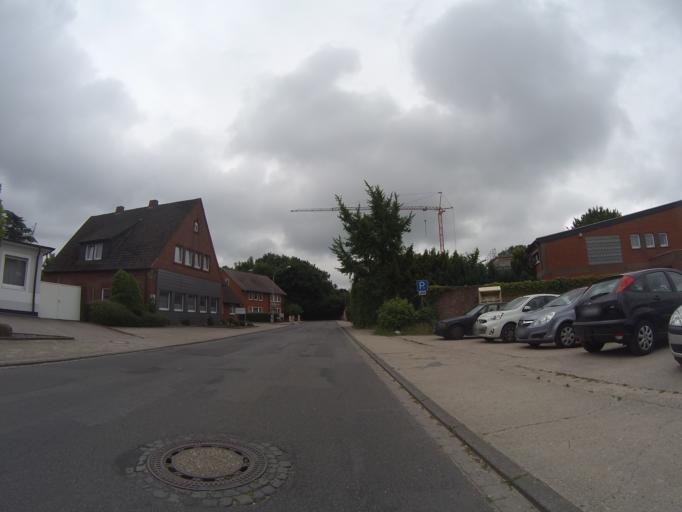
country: DE
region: Lower Saxony
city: Meppen
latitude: 52.6968
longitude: 7.2921
